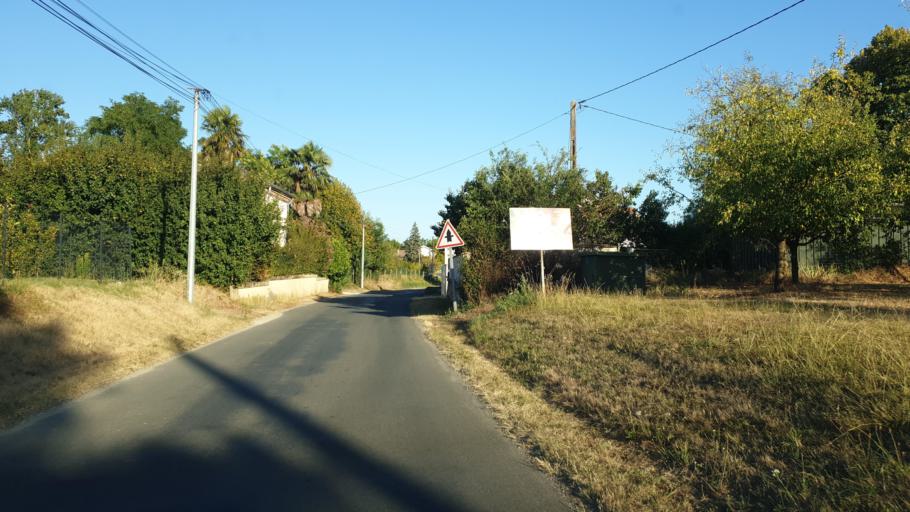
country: FR
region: Aquitaine
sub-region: Departement du Lot-et-Garonne
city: Castelmoron-sur-Lot
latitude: 44.3929
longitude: 0.5024
